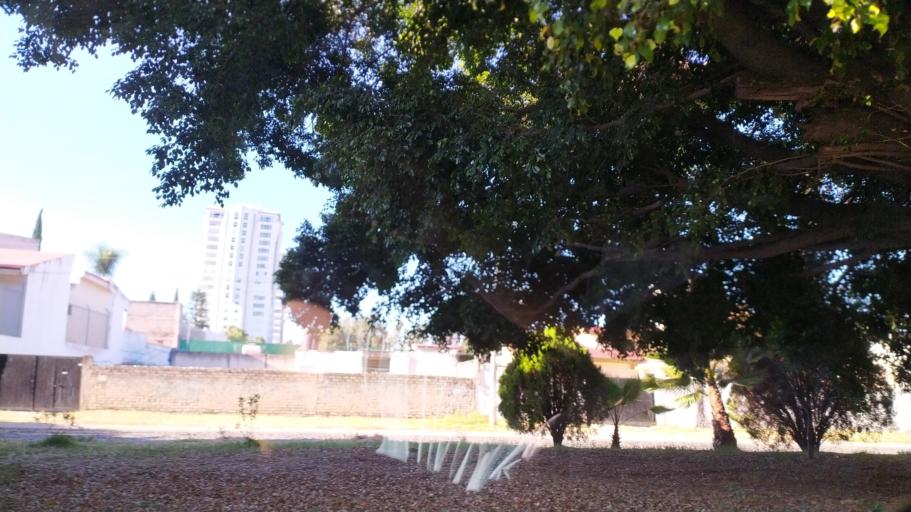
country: MX
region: Jalisco
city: Guadalajara
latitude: 20.6668
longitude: -103.4334
